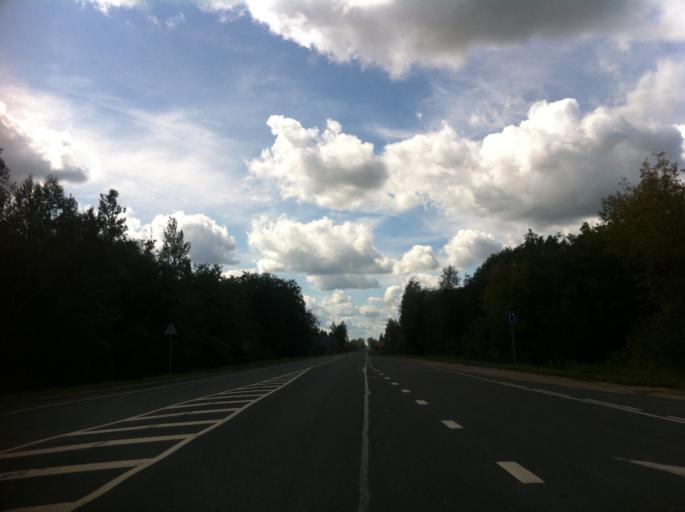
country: RU
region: Pskov
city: Pskov
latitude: 57.7661
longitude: 28.1093
